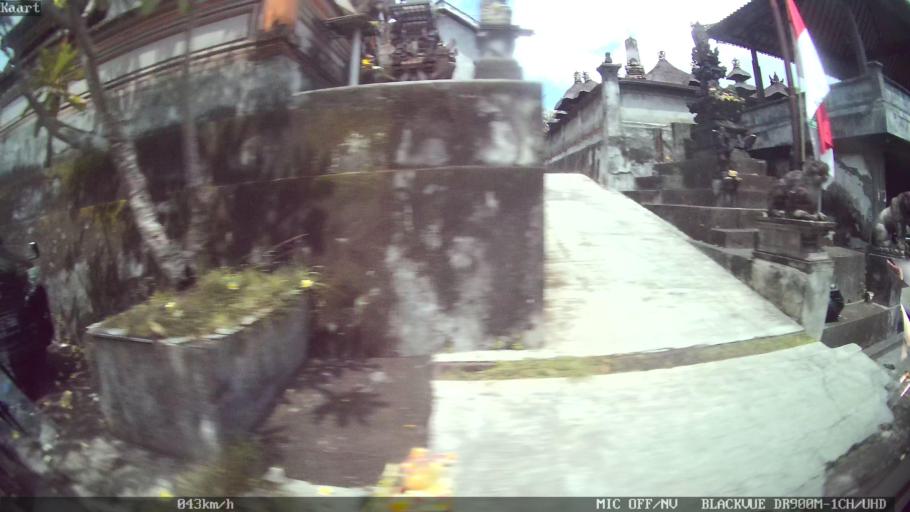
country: ID
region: Bali
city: Banjar Tebongkang
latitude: -8.5527
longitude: 115.2831
